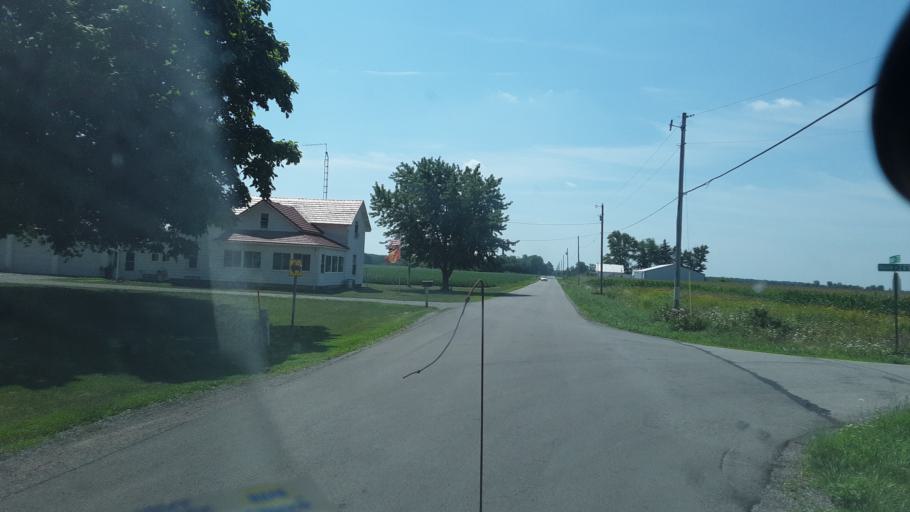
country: US
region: Ohio
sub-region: Hancock County
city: Findlay
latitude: 41.0069
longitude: -83.5160
